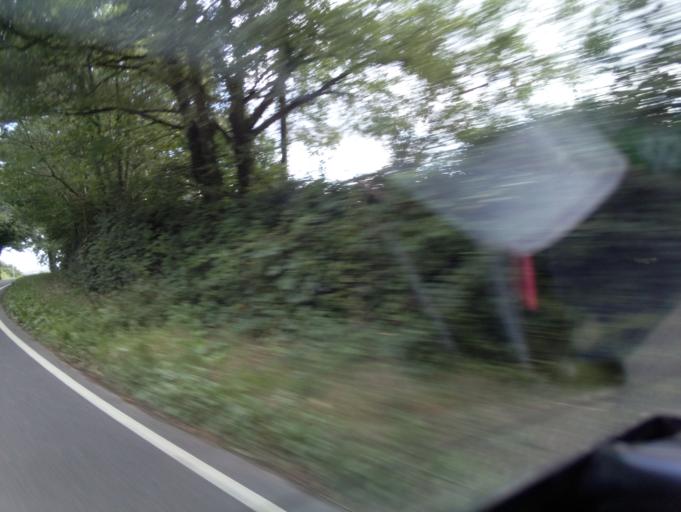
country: GB
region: England
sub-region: Devon
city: Honiton
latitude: 50.7488
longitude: -3.2085
